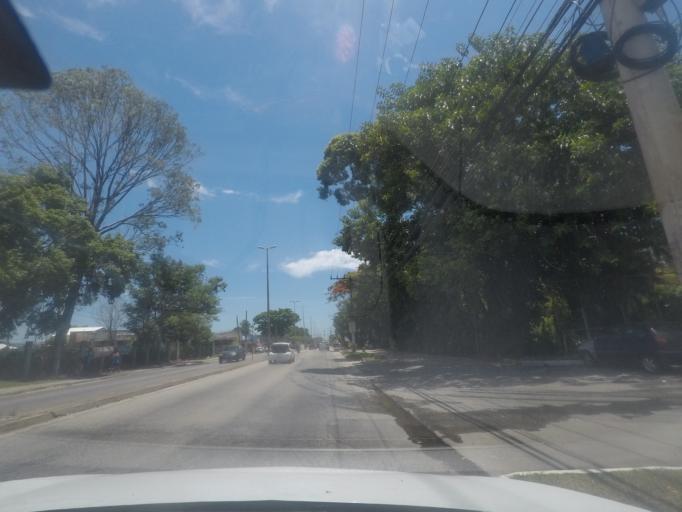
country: BR
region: Rio de Janeiro
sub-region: Itaguai
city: Itaguai
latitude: -22.9048
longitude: -43.6835
